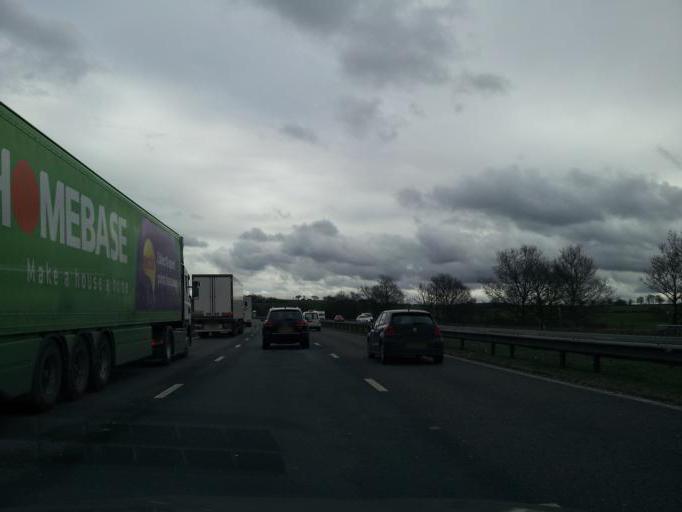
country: GB
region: England
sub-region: Staffordshire
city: Audley
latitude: 53.0016
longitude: -2.3237
